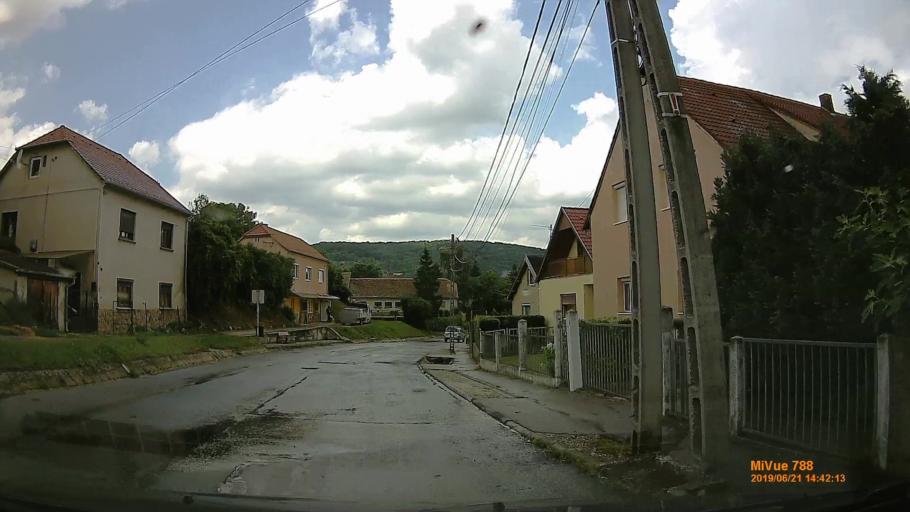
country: HU
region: Baranya
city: Hosszuheteny
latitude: 46.1219
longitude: 18.3105
